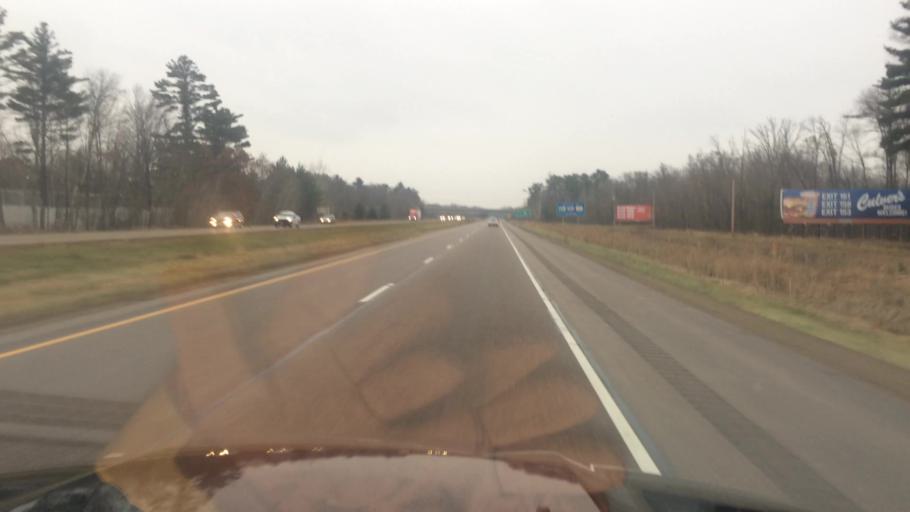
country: US
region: Wisconsin
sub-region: Portage County
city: Stevens Point
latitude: 44.5571
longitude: -89.5878
